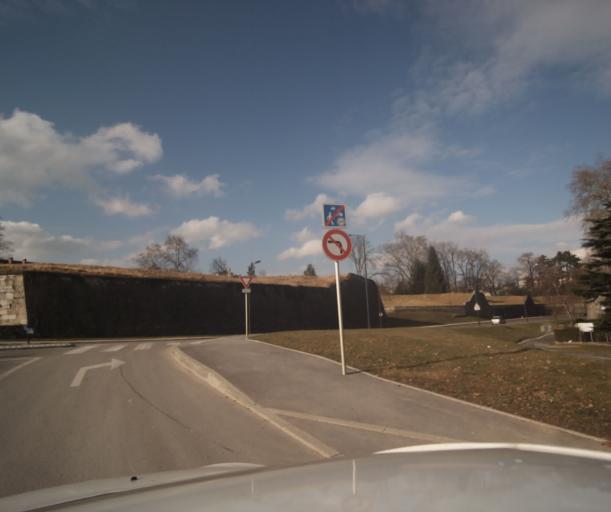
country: FR
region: Franche-Comte
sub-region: Departement du Doubs
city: Besancon
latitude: 47.2423
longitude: 6.0181
